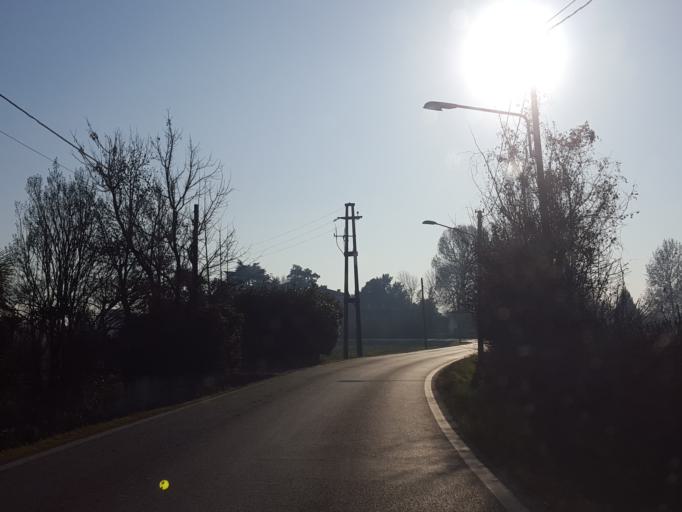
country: IT
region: Veneto
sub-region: Provincia di Vicenza
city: Villaggio Montegrappa
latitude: 45.5543
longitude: 11.6034
